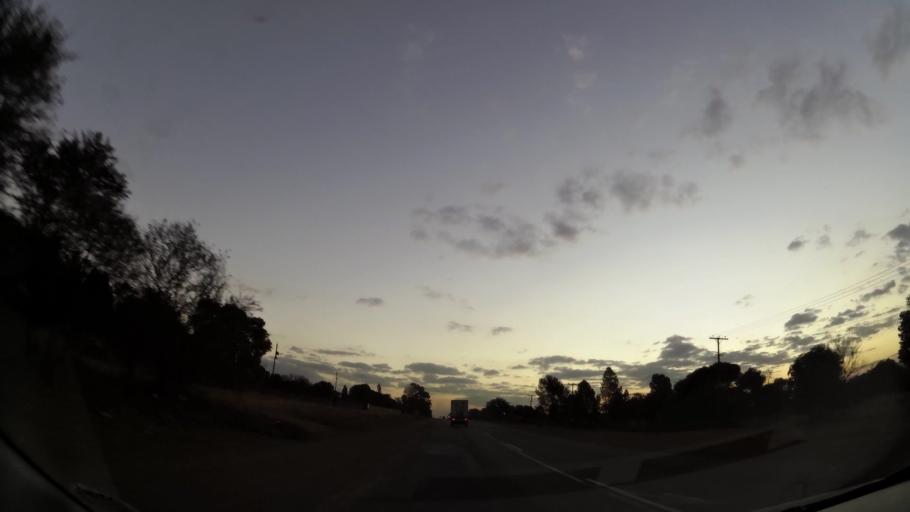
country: ZA
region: Gauteng
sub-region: West Rand District Municipality
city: Krugersdorp
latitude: -26.0695
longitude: 27.6796
